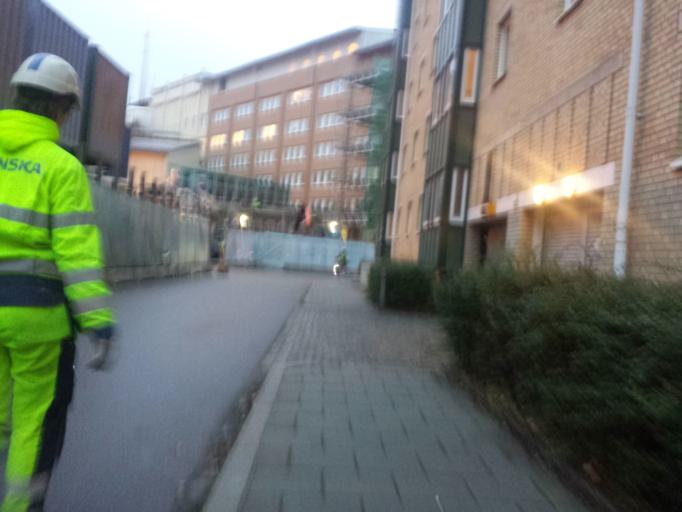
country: SE
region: Skane
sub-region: Malmo
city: Malmoe
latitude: 55.6067
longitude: 13.0159
